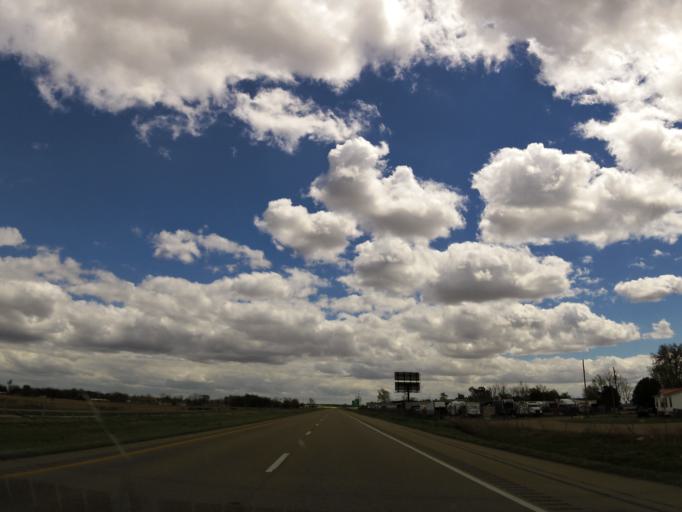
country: US
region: Arkansas
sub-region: Poinsett County
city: Marked Tree
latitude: 35.4936
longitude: -90.3743
